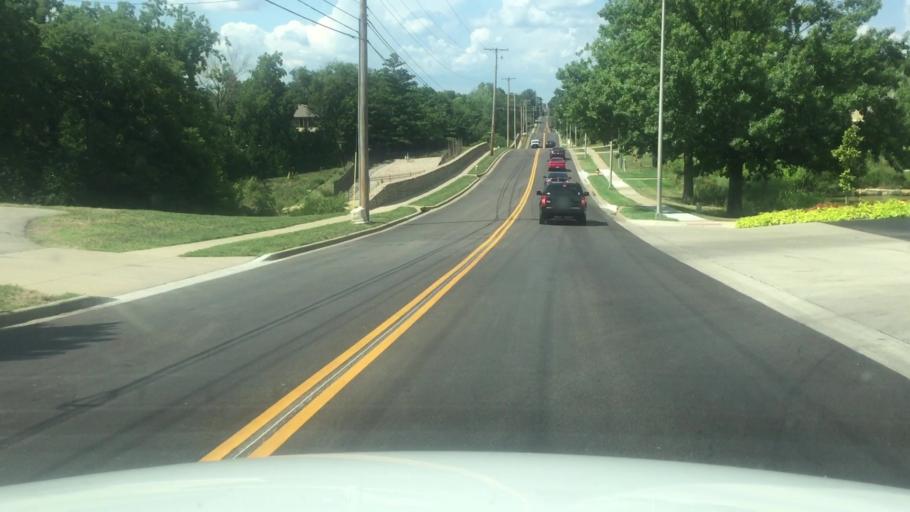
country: US
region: Kansas
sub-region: Johnson County
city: Lenexa
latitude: 38.9739
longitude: -94.7423
